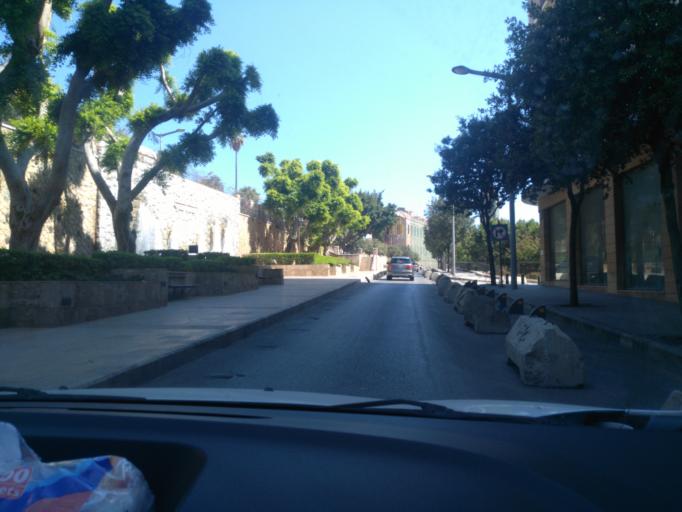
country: LB
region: Beyrouth
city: Beirut
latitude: 33.8957
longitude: 35.5022
